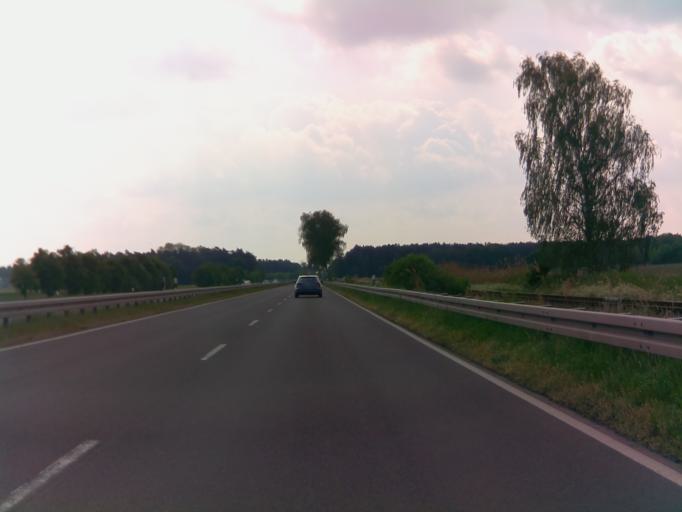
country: DE
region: Saxony-Anhalt
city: Hassel
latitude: 52.5747
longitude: 11.9163
